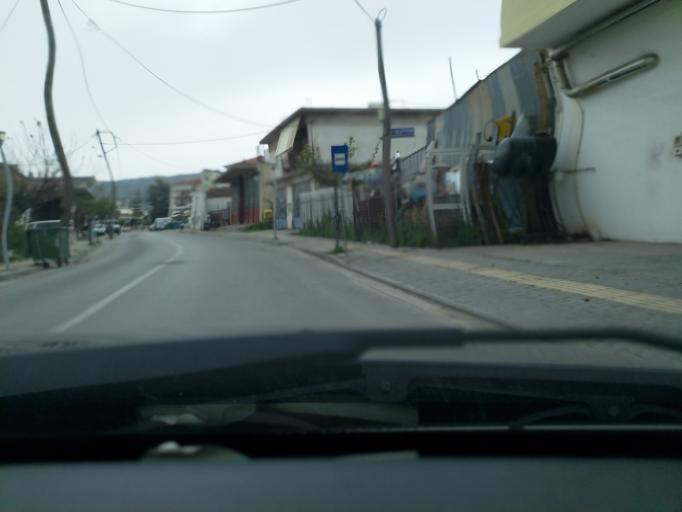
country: GR
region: Crete
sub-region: Nomos Chanias
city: Chania
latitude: 35.4971
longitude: 24.0217
